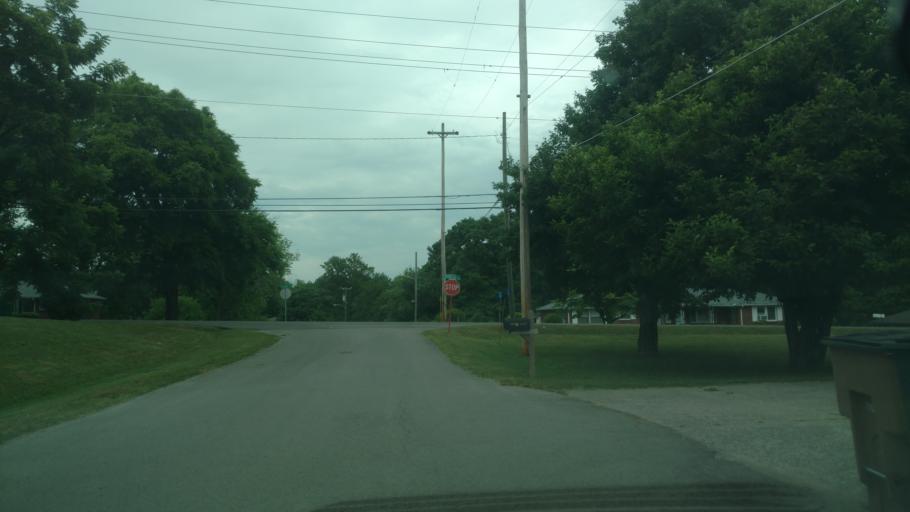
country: US
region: Tennessee
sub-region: Davidson County
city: Nashville
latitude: 36.1954
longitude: -86.7147
